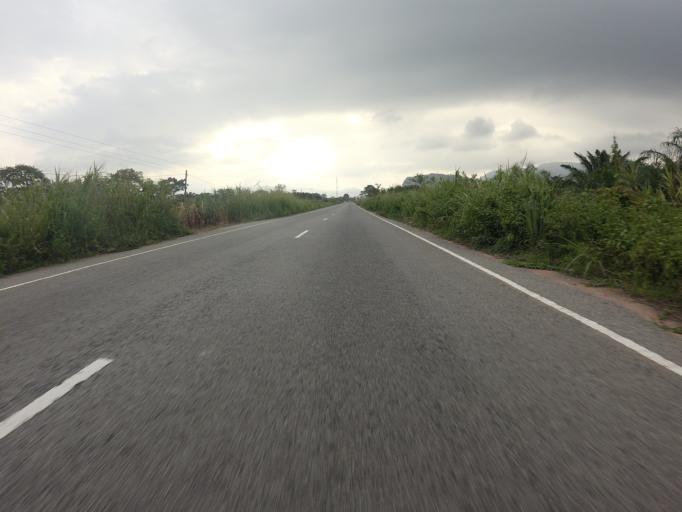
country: GH
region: Volta
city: Ho
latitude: 6.7801
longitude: 0.4675
